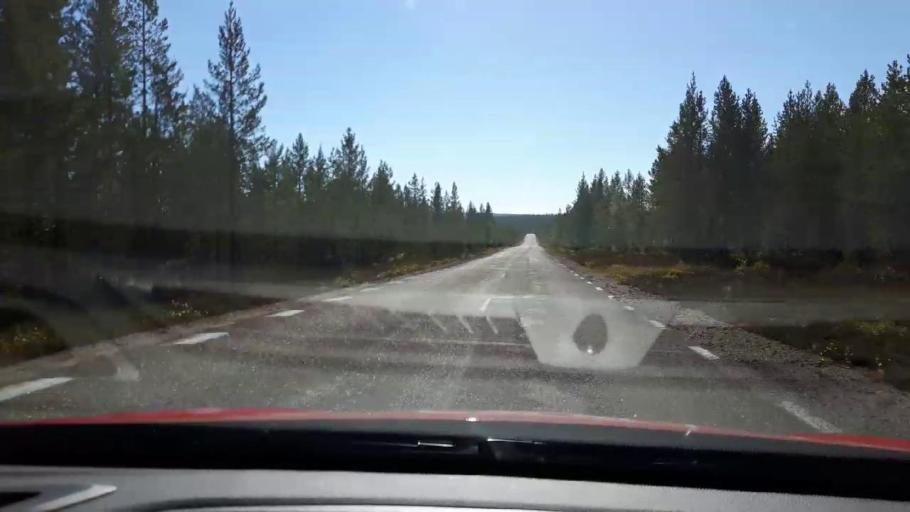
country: SE
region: Jaemtland
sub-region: Harjedalens Kommun
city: Sveg
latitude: 61.7196
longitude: 14.1680
